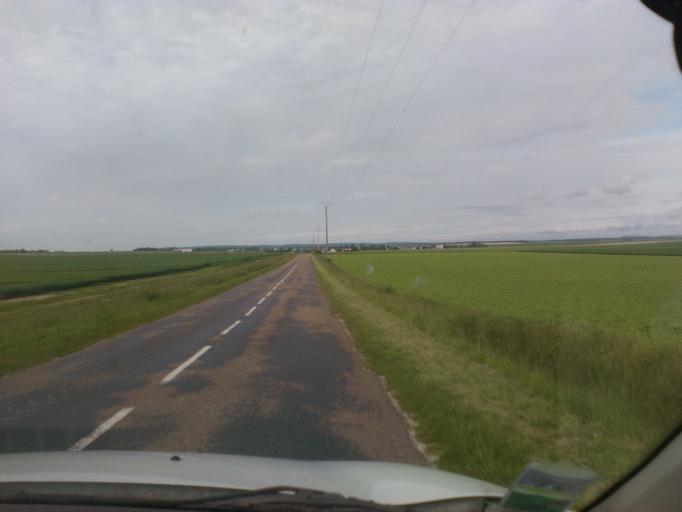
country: FR
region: Champagne-Ardenne
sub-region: Departement de l'Aube
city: Marigny-le-Chatel
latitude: 48.3851
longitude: 3.7968
